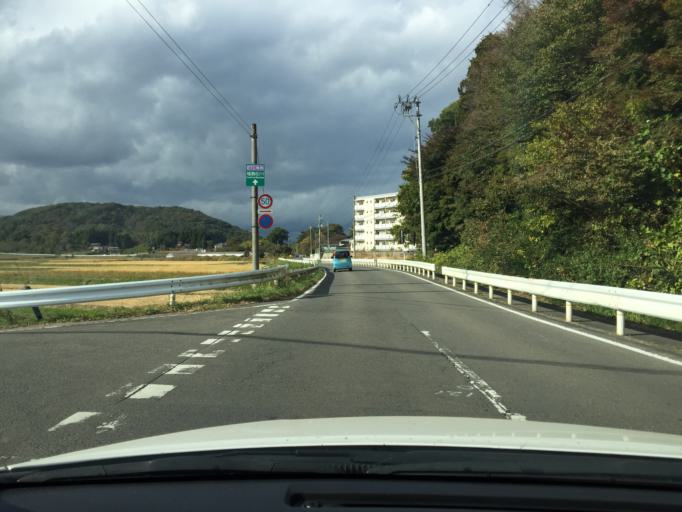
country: JP
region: Fukushima
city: Nihommatsu
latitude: 37.6584
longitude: 140.4561
